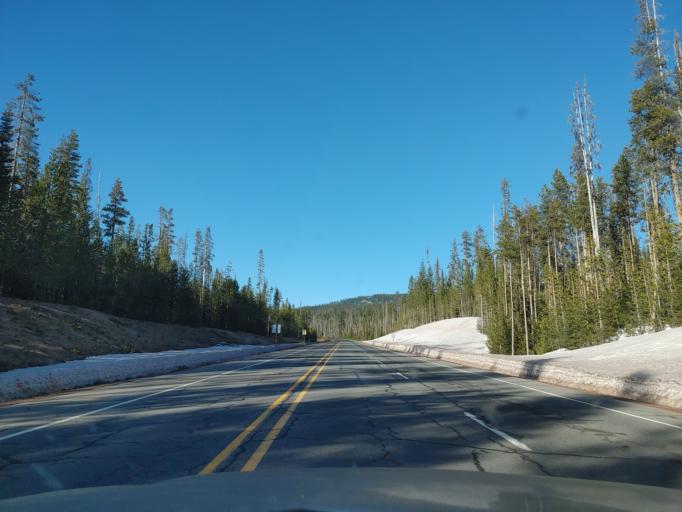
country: US
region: Oregon
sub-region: Lane County
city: Oakridge
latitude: 43.1288
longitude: -122.1301
